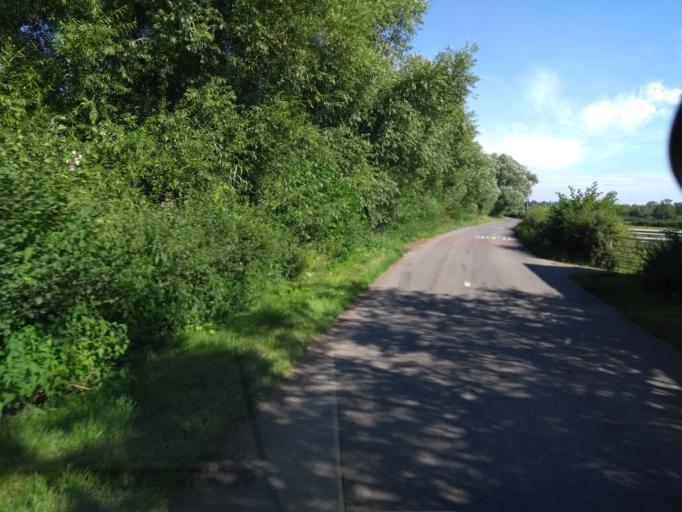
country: GB
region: England
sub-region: Somerset
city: Ilchester
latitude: 51.0919
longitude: -2.6425
